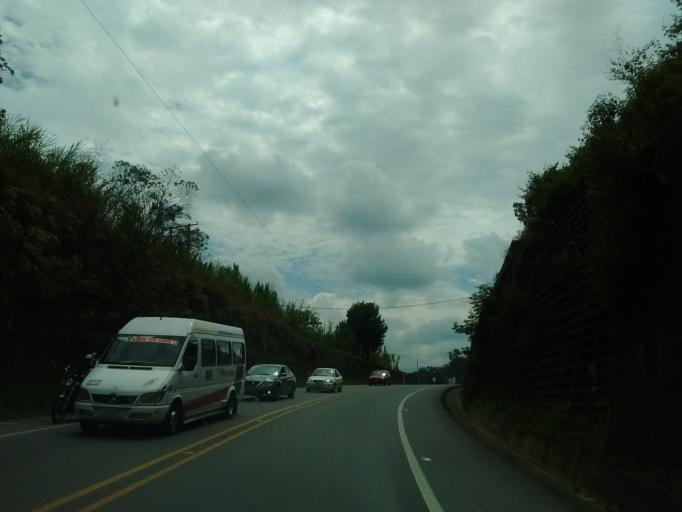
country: CO
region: Cauca
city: Cajibio
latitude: 2.5487
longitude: -76.5634
